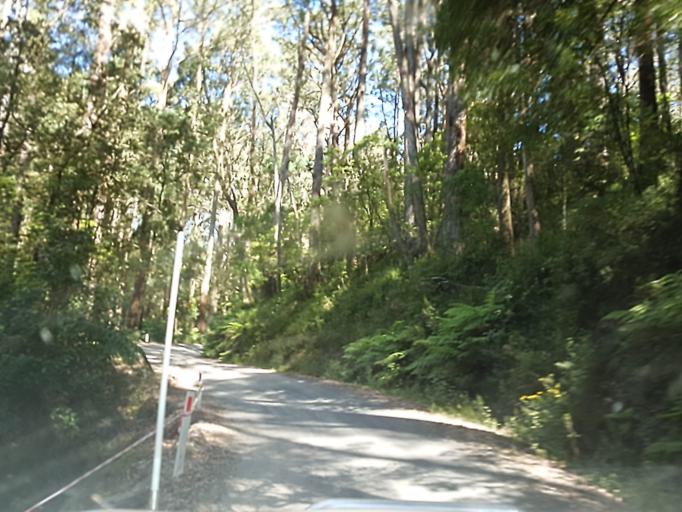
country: AU
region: Victoria
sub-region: Colac-Otway
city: Apollo Bay
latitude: -38.6780
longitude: 143.3596
